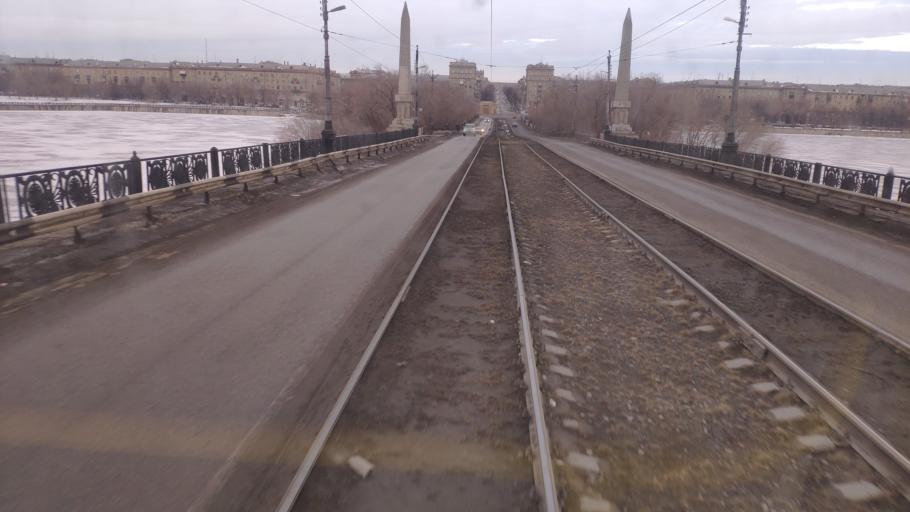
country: RU
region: Chelyabinsk
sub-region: Gorod Magnitogorsk
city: Magnitogorsk
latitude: 53.4222
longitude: 59.0085
